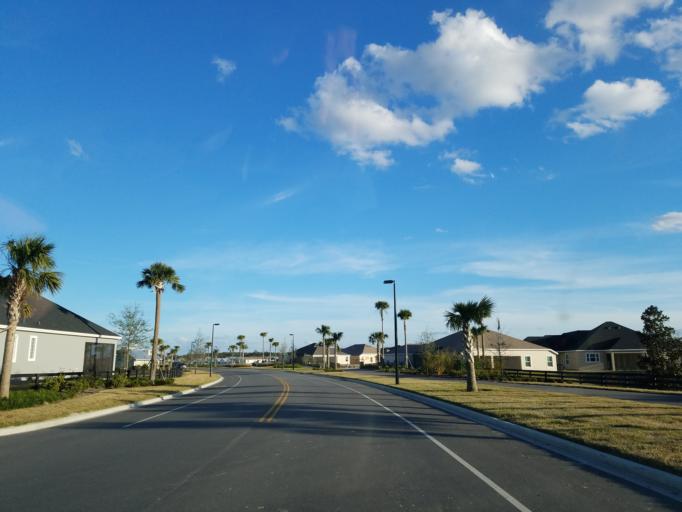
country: US
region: Florida
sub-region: Sumter County
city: Lake Panasoffkee
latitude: 28.7937
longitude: -82.0346
